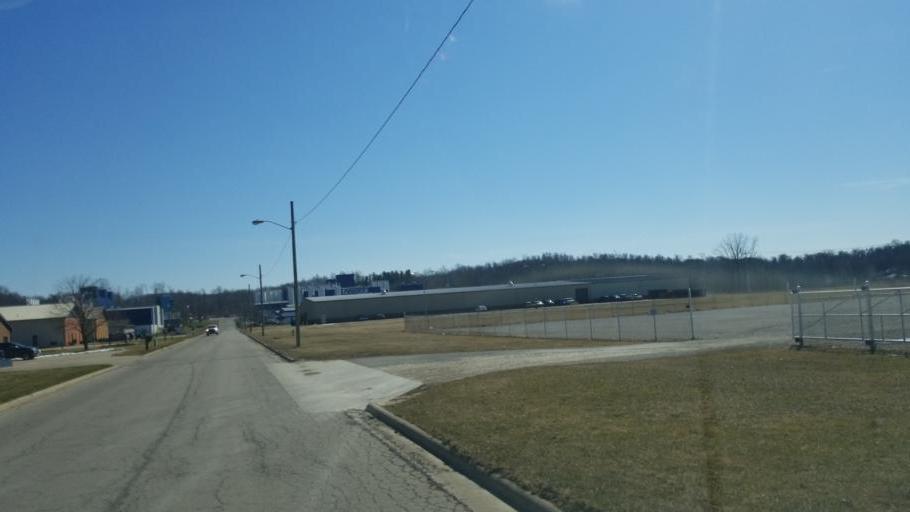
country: US
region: Ohio
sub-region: Richland County
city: Lexington
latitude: 40.6787
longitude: -82.5667
